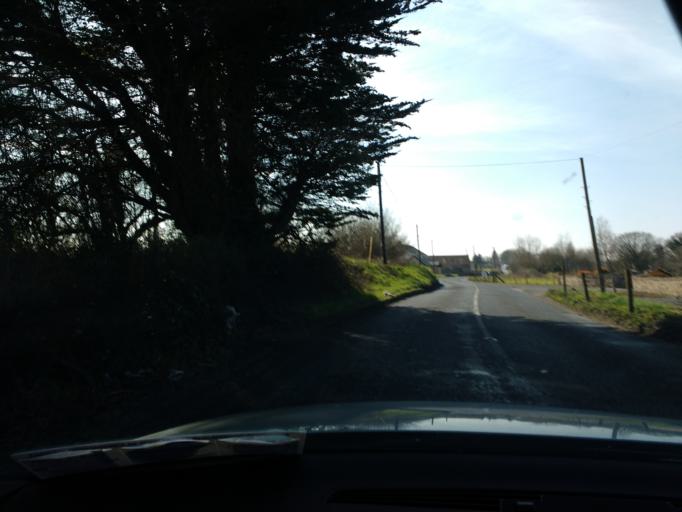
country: IE
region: Munster
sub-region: County Limerick
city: Castleconnell
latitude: 52.6977
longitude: -8.4617
